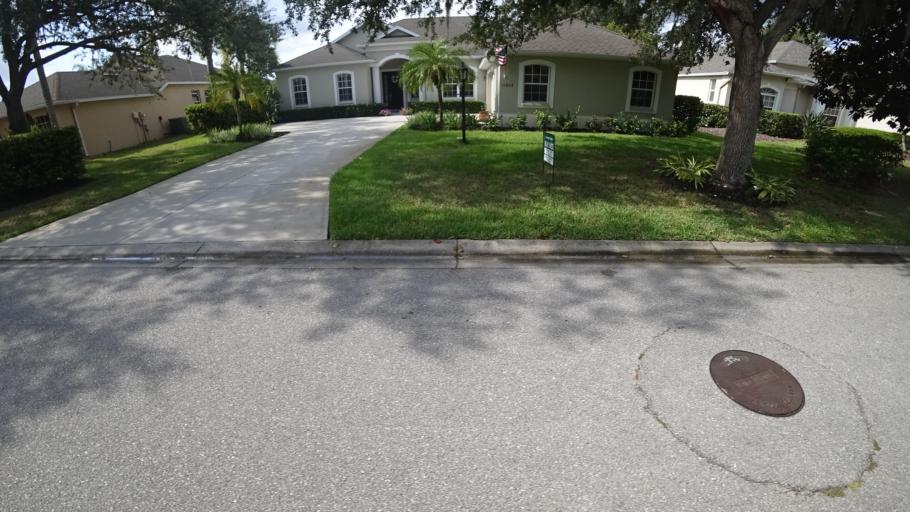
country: US
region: Florida
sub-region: Sarasota County
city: The Meadows
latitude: 27.4223
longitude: -82.4237
